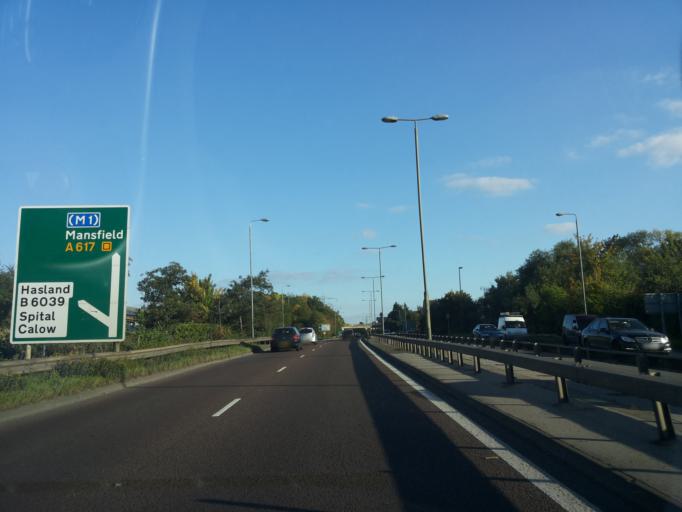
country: GB
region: England
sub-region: Derbyshire
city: Chesterfield
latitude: 53.2305
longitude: -1.4210
